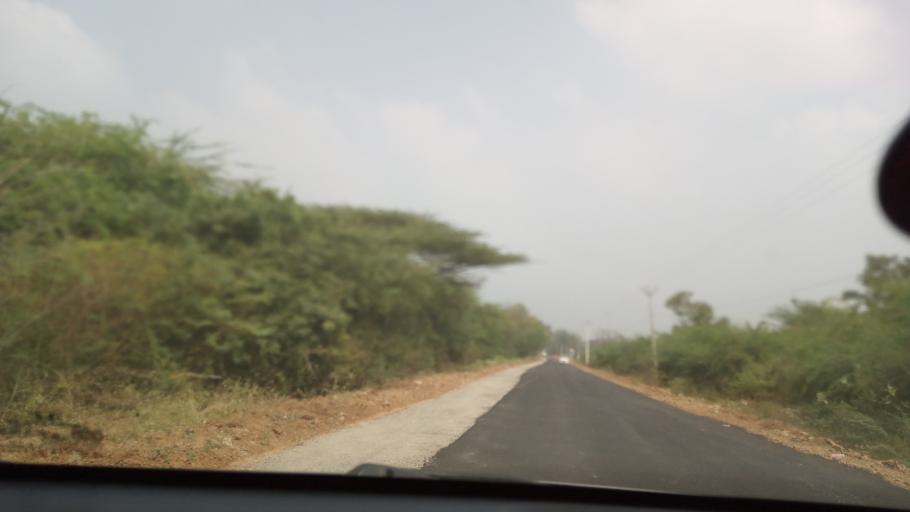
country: IN
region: Tamil Nadu
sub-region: Erode
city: Sathyamangalam
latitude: 11.5473
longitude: 77.1395
